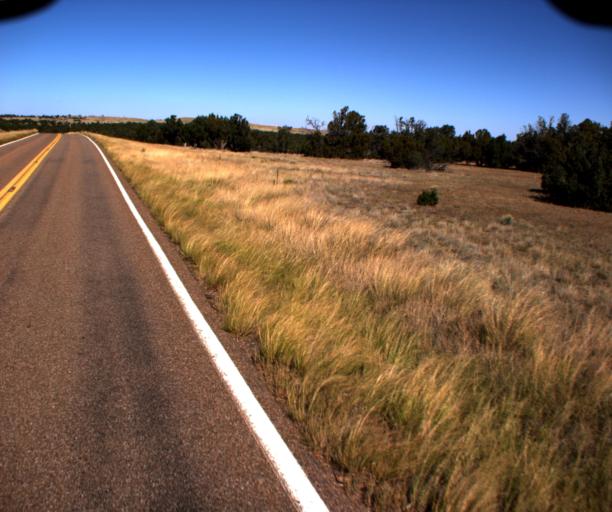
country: US
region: Arizona
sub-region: Navajo County
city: Heber-Overgaard
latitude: 34.4564
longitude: -110.4646
